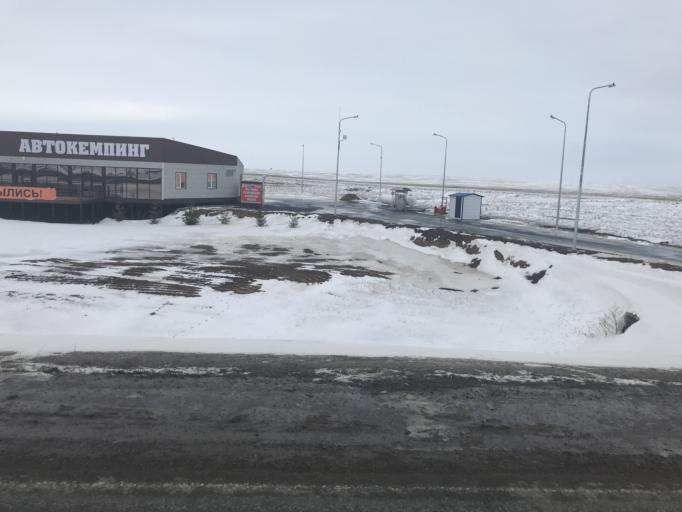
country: KZ
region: Batys Qazaqstan
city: Oral
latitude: 51.4035
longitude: 51.2972
